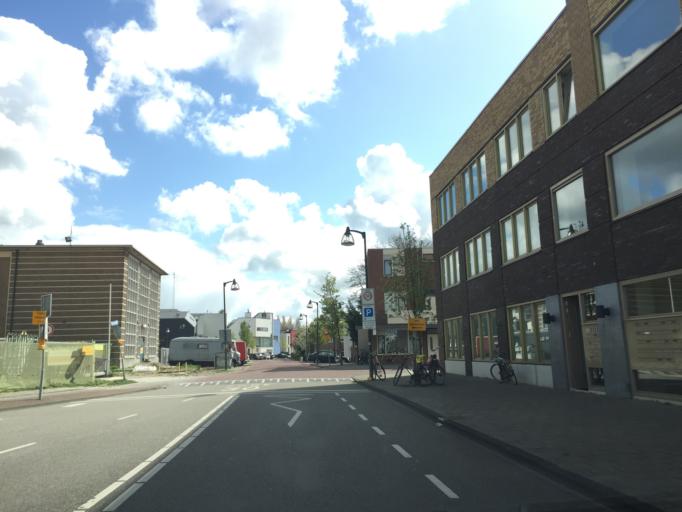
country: NL
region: South Holland
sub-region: Gemeente Leiden
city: Leiden
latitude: 52.1684
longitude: 4.4927
